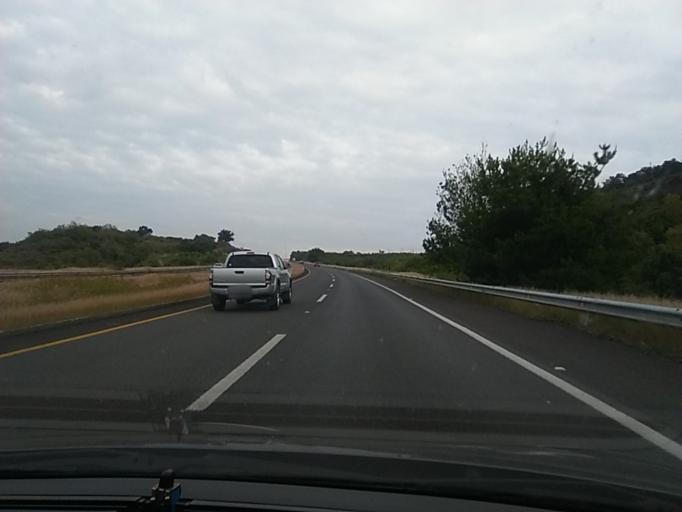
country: MX
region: Michoacan
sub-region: Puruandiro
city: San Lorenzo
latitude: 19.9603
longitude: -101.6863
